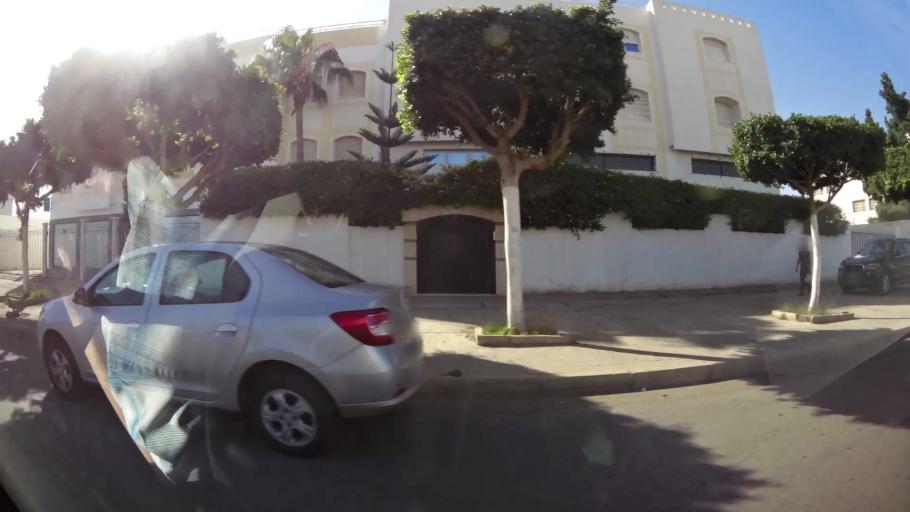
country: MA
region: Souss-Massa-Draa
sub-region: Inezgane-Ait Mellou
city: Inezgane
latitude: 30.3849
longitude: -9.5171
